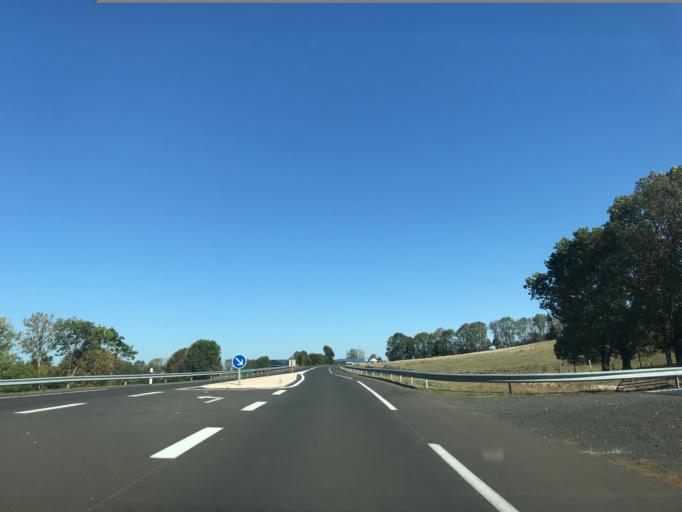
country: FR
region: Auvergne
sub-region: Departement du Puy-de-Dome
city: Gelles
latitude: 45.6962
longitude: 2.8049
